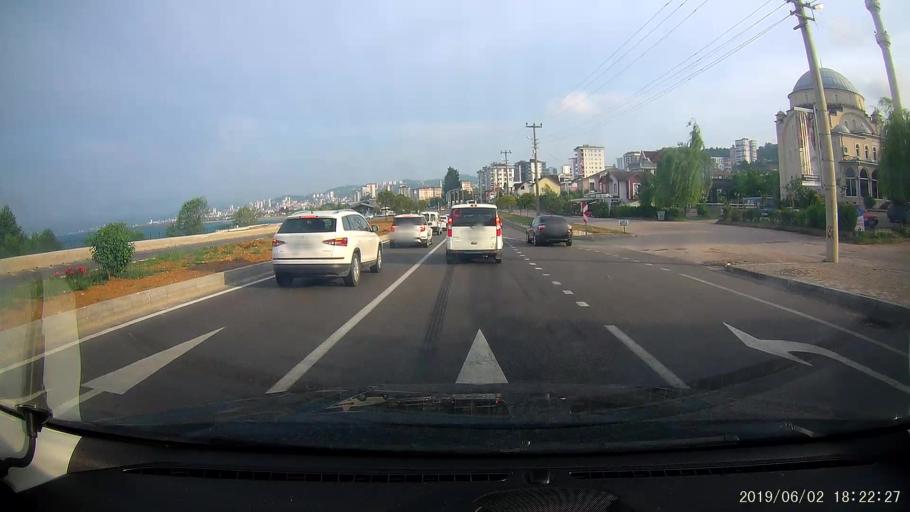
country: TR
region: Ordu
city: Fatsa
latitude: 41.0571
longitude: 37.4772
